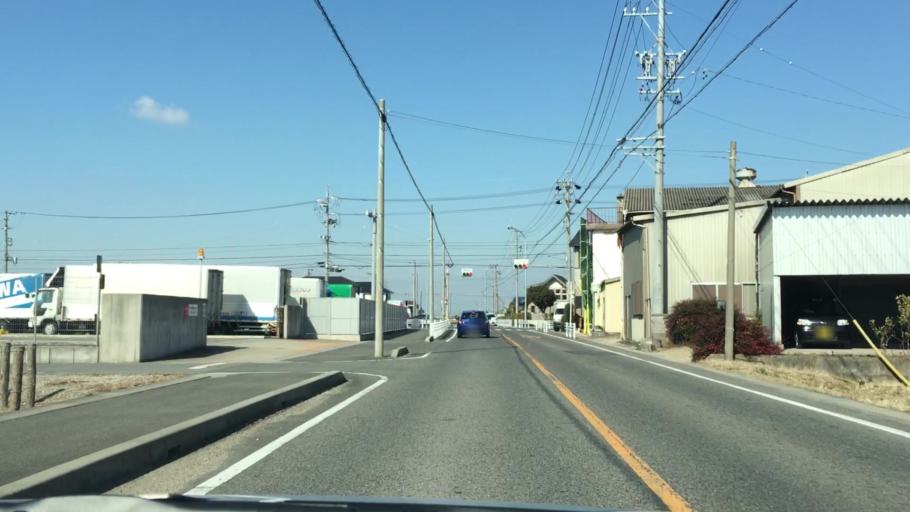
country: JP
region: Aichi
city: Anjo
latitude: 34.9755
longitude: 137.1200
